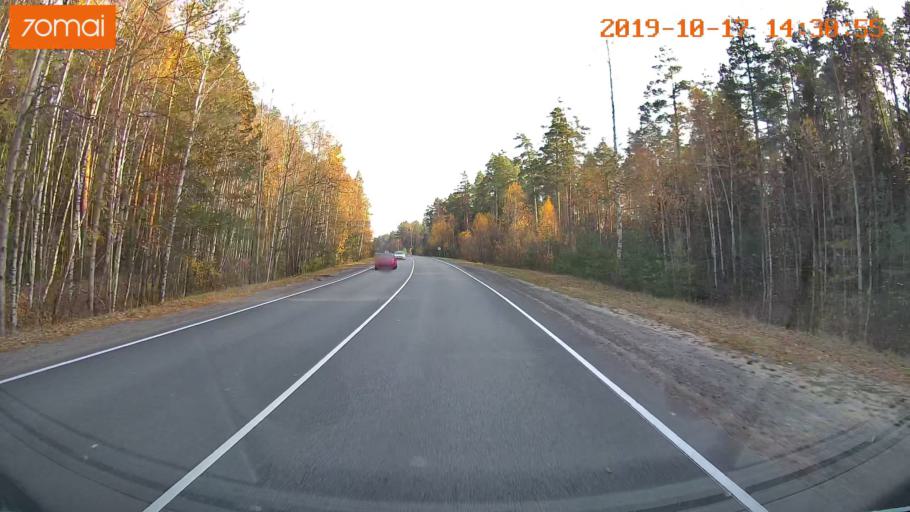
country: RU
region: Rjazan
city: Solotcha
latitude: 54.9415
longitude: 39.9521
